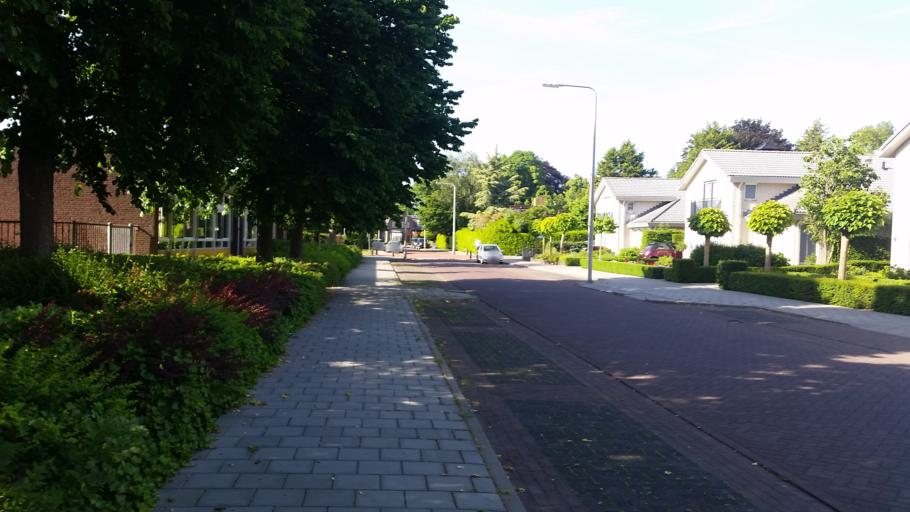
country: NL
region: Gelderland
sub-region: Gemeente Geldermalsen
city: Geldermalsen
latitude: 51.8810
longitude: 5.2939
